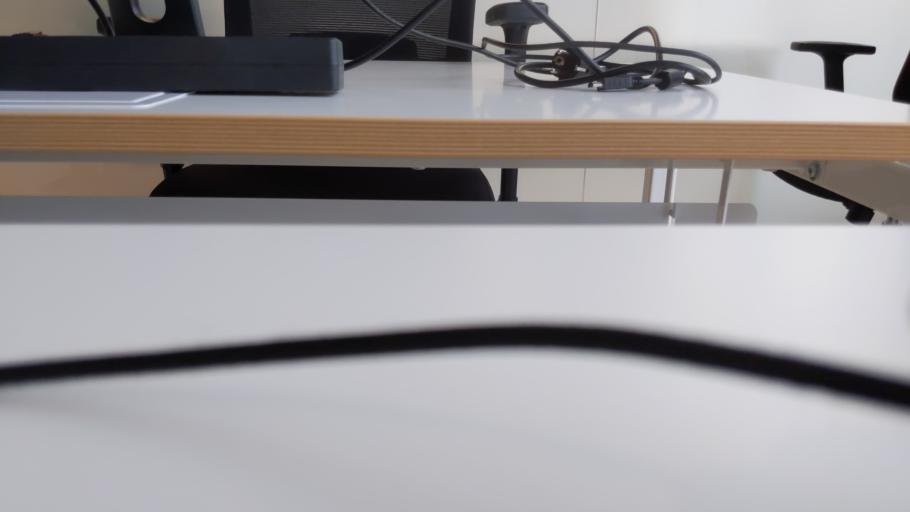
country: RU
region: Moskovskaya
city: Shevlyakovo
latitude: 56.4202
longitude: 36.9609
